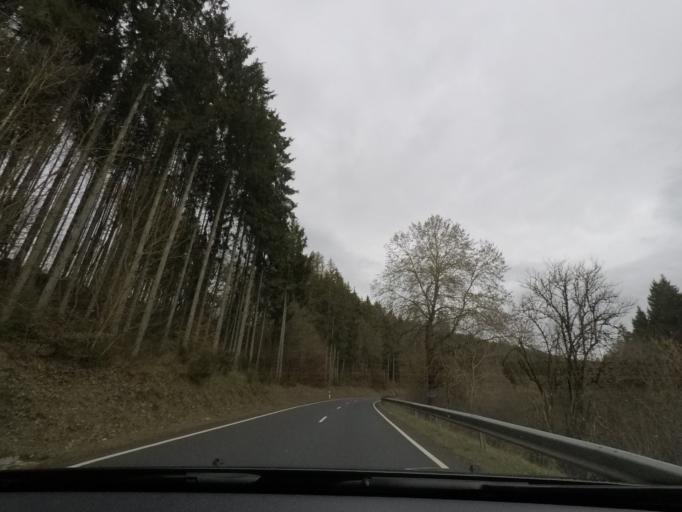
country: LU
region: Diekirch
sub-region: Canton de Wiltz
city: Winseler
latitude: 49.9951
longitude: 5.8579
